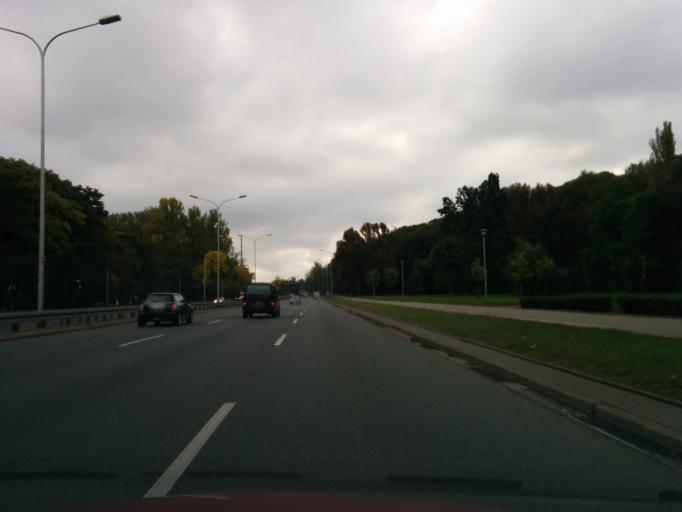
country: PL
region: Masovian Voivodeship
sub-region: Warszawa
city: Zoliborz
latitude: 52.2646
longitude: 21.0039
